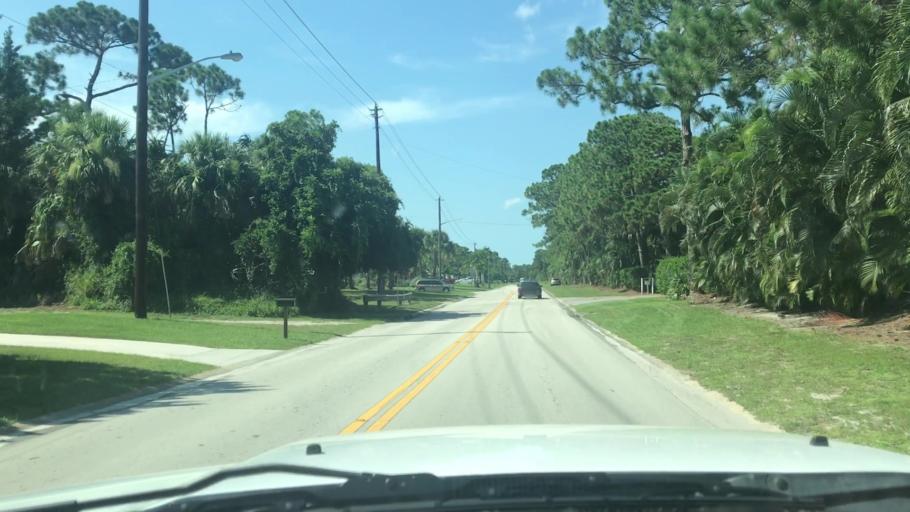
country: US
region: Florida
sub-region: Indian River County
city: Florida Ridge
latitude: 27.5646
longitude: -80.3980
